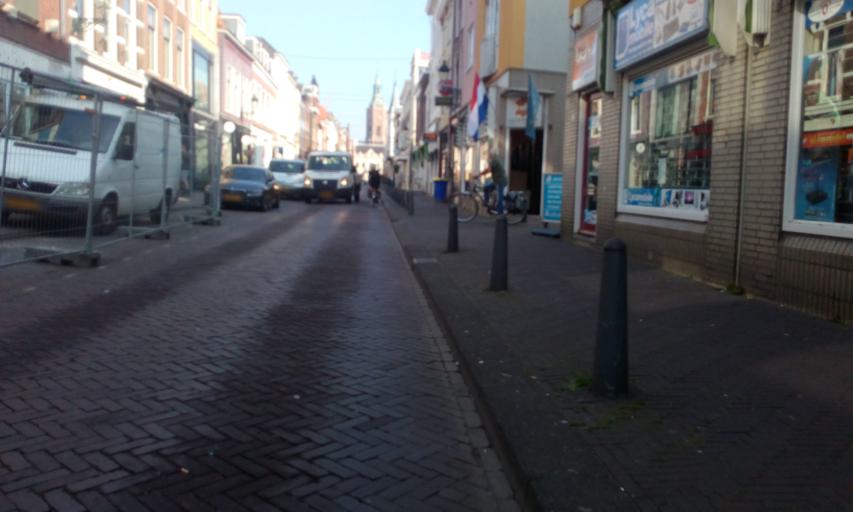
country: NL
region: South Holland
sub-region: Gemeente Den Haag
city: The Hague
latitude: 52.0731
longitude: 4.3105
